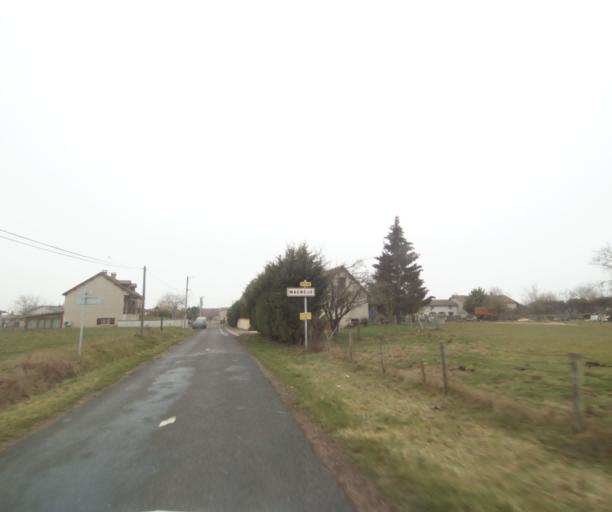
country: FR
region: Champagne-Ardenne
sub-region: Departement de la Haute-Marne
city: Wassy
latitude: 48.5127
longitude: 5.0104
